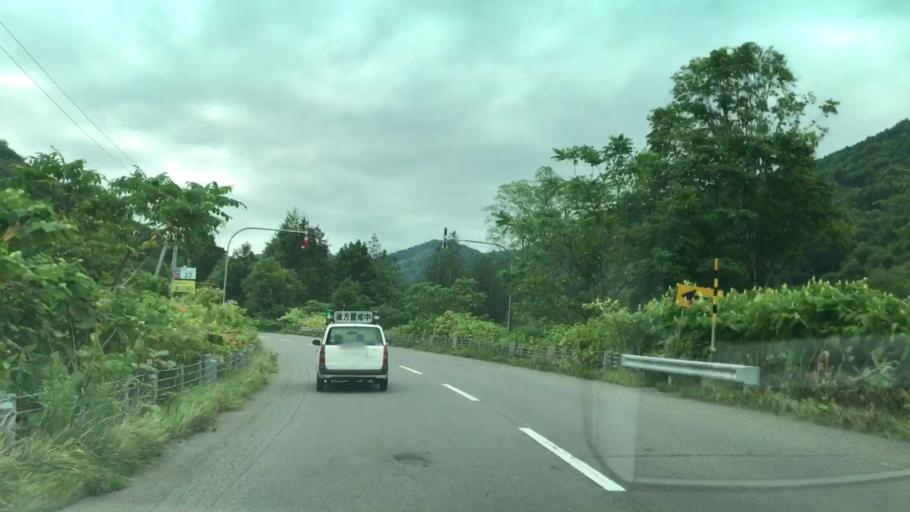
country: JP
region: Hokkaido
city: Yoichi
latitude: 43.0237
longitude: 140.8662
